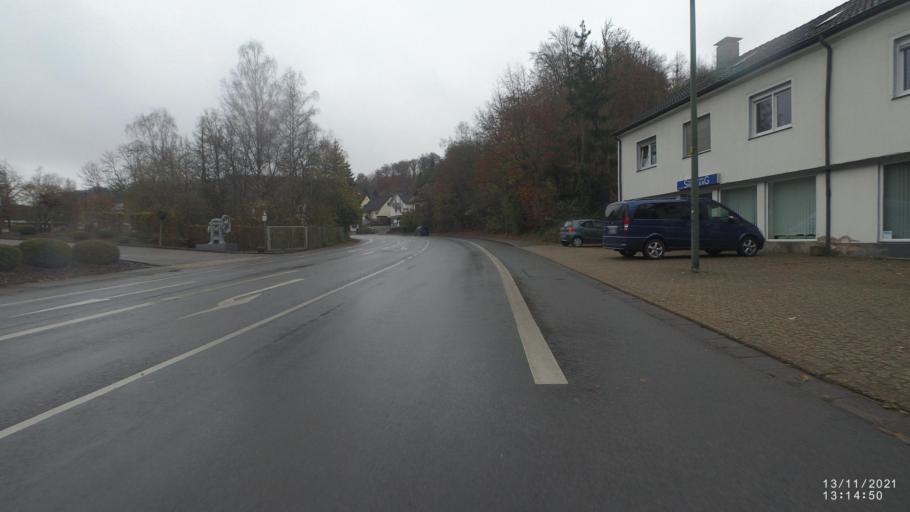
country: DE
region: North Rhine-Westphalia
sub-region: Regierungsbezirk Arnsberg
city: Luedenscheid
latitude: 51.2449
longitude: 7.6206
